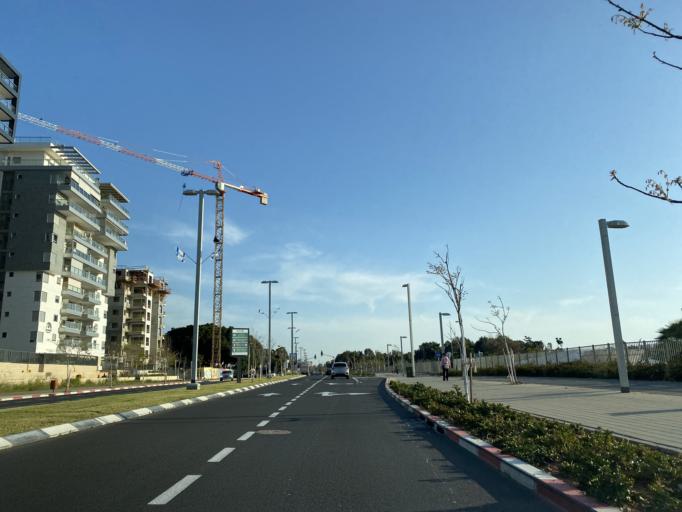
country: IL
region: Tel Aviv
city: Herzliyya
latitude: 32.1772
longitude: 34.8300
